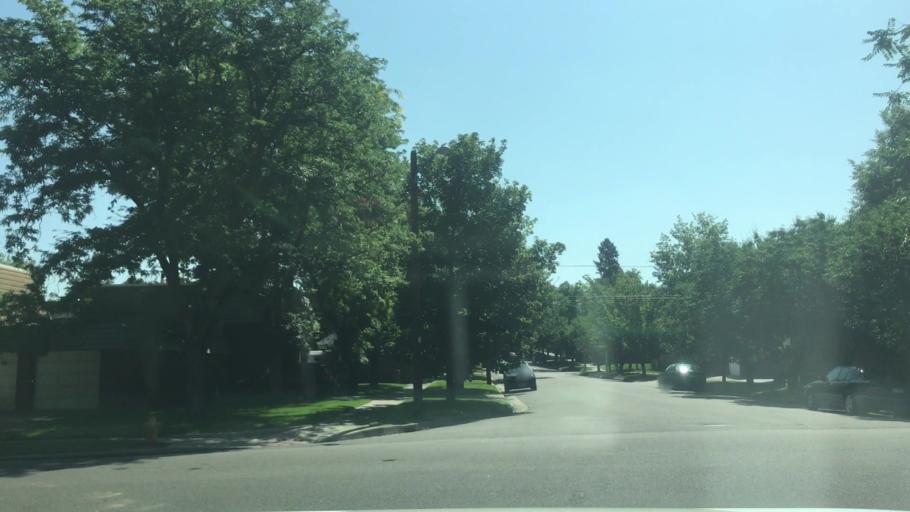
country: US
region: Colorado
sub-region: Denver County
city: Denver
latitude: 39.7003
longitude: -104.9783
